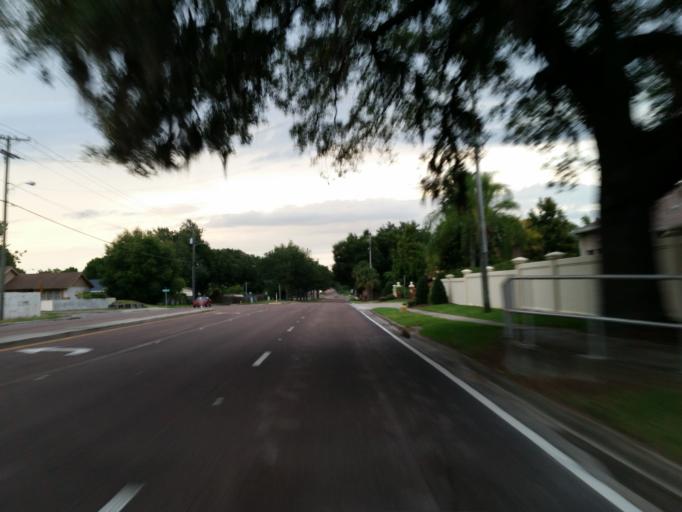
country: US
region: Florida
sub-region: Hillsborough County
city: Brandon
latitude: 27.9126
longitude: -82.2939
